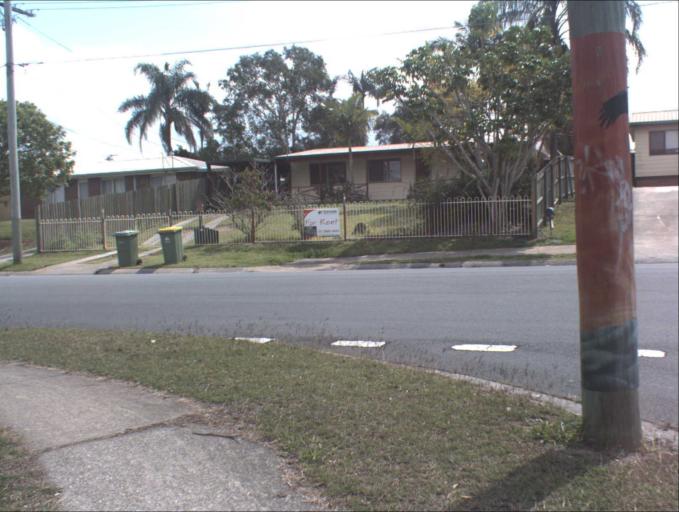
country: AU
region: Queensland
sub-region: Logan
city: Woodridge
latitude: -27.6608
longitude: 153.0625
